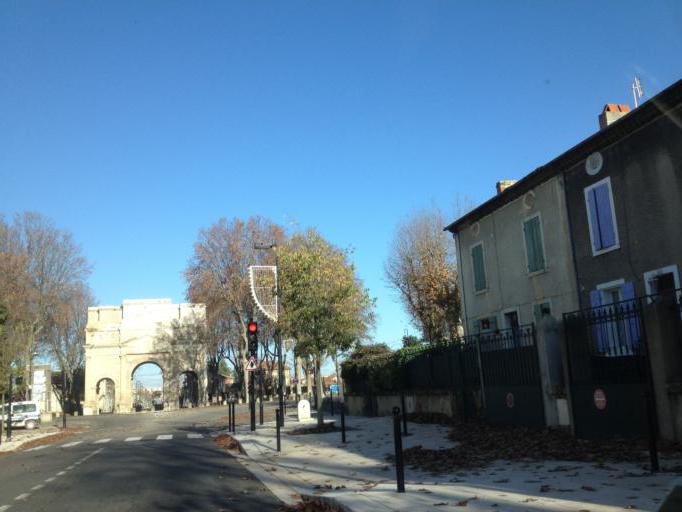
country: FR
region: Provence-Alpes-Cote d'Azur
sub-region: Departement du Vaucluse
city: Orange
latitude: 44.1411
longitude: 4.8052
